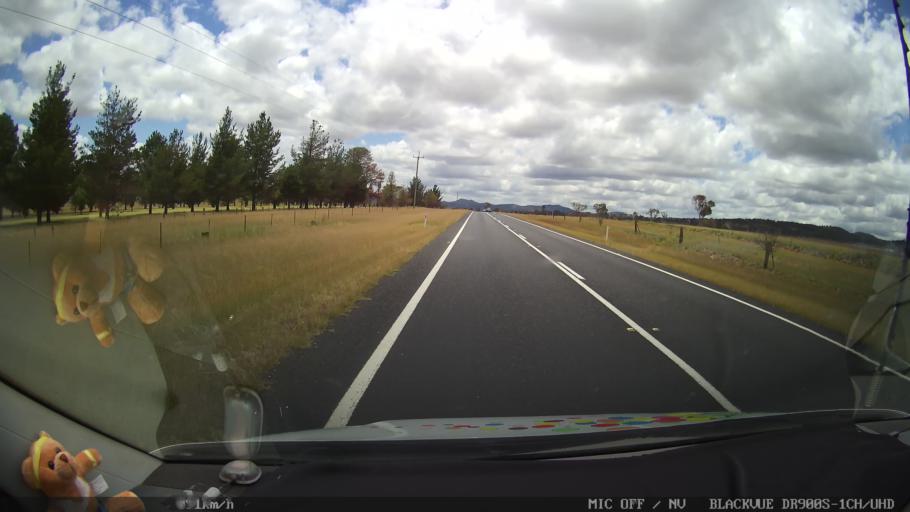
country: AU
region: New South Wales
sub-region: Glen Innes Severn
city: Glen Innes
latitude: -29.4296
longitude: 151.8559
